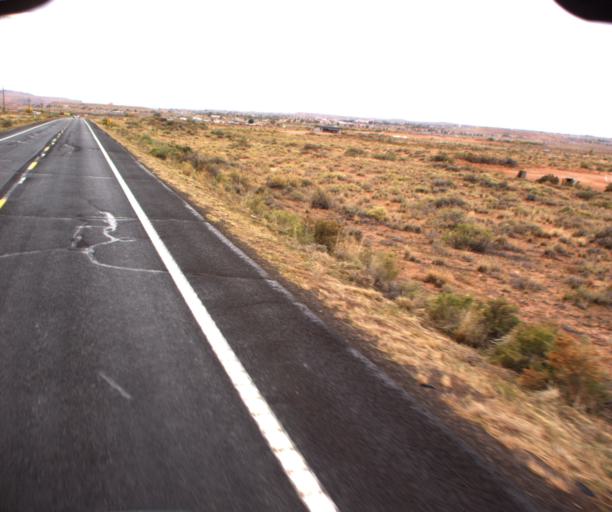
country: US
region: Arizona
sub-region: Coconino County
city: Tuba City
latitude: 36.1295
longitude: -111.1918
